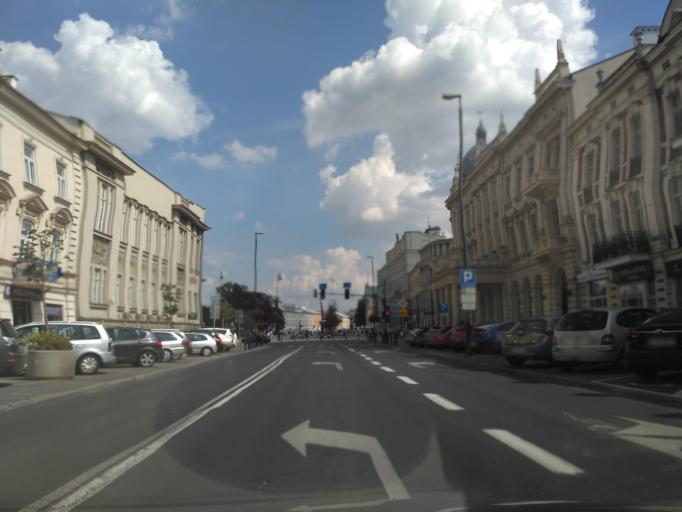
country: PL
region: Lublin Voivodeship
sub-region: Powiat lubelski
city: Lublin
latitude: 51.2478
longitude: 22.5568
